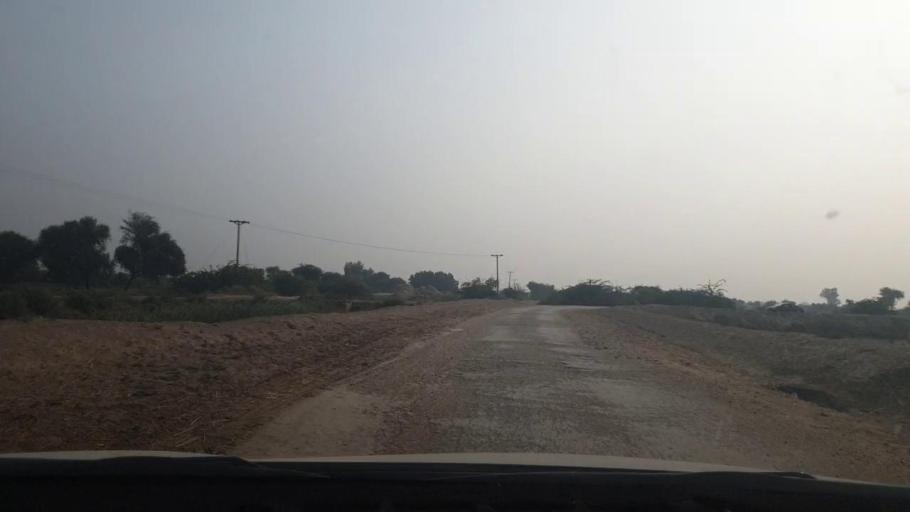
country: PK
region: Sindh
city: Bulri
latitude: 24.7865
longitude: 68.4254
